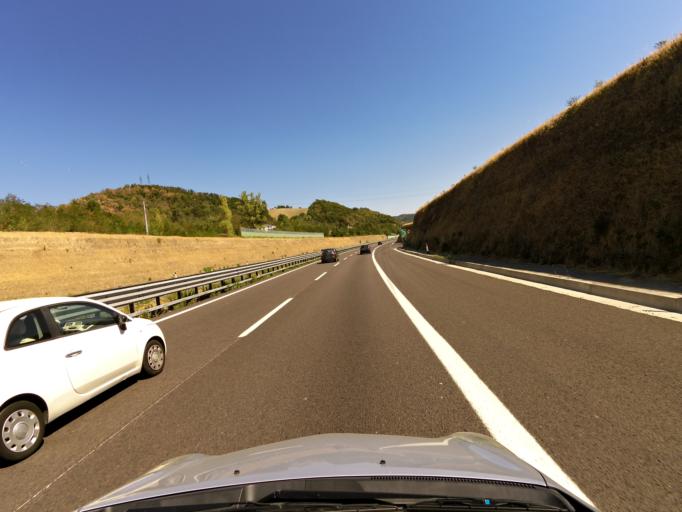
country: IT
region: Emilia-Romagna
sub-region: Provincia di Bologna
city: Grizzana
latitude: 44.2683
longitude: 11.1882
